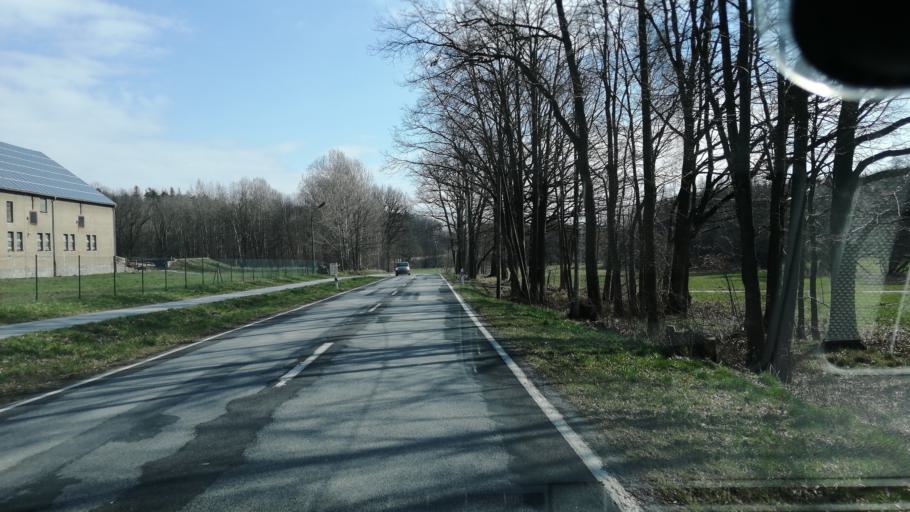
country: DE
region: Saxony
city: Grossschweidnitz
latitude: 51.0843
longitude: 14.6231
